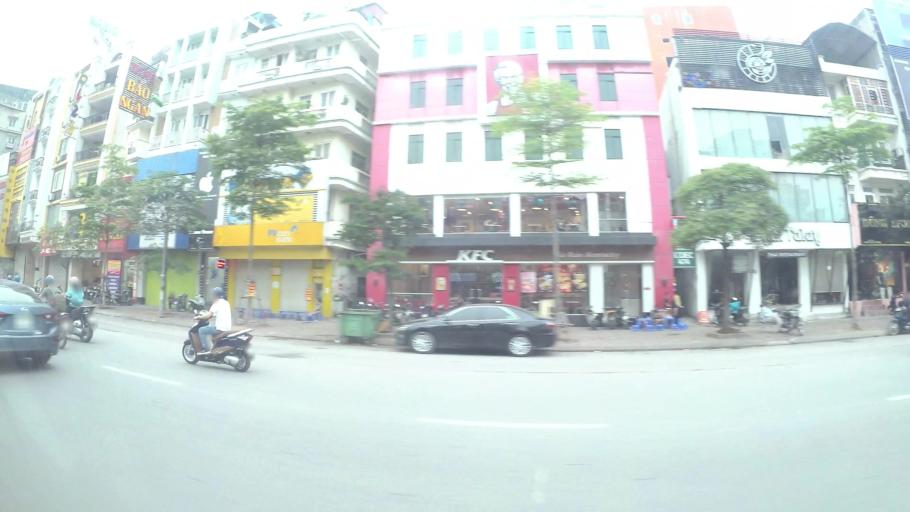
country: VN
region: Ha Noi
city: Dong Da
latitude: 21.0168
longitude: 105.8316
